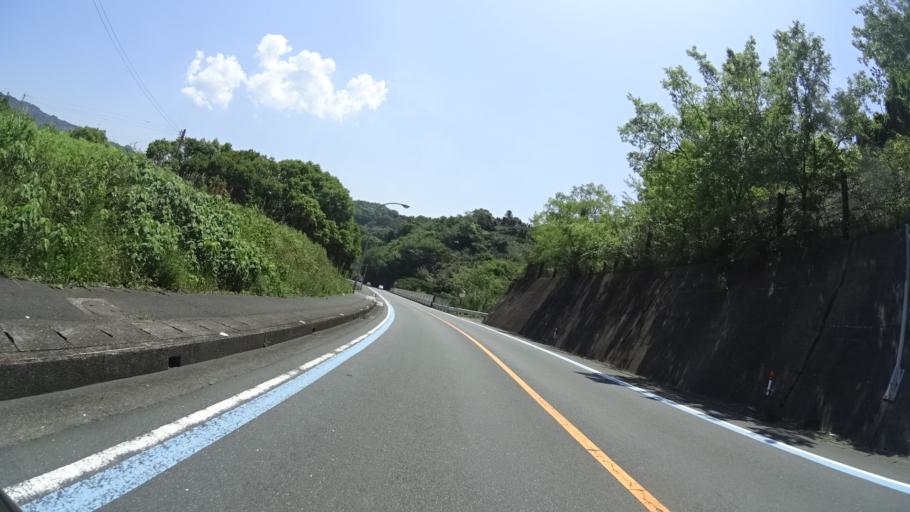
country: JP
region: Ehime
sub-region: Nishiuwa-gun
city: Ikata-cho
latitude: 33.4897
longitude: 132.3867
